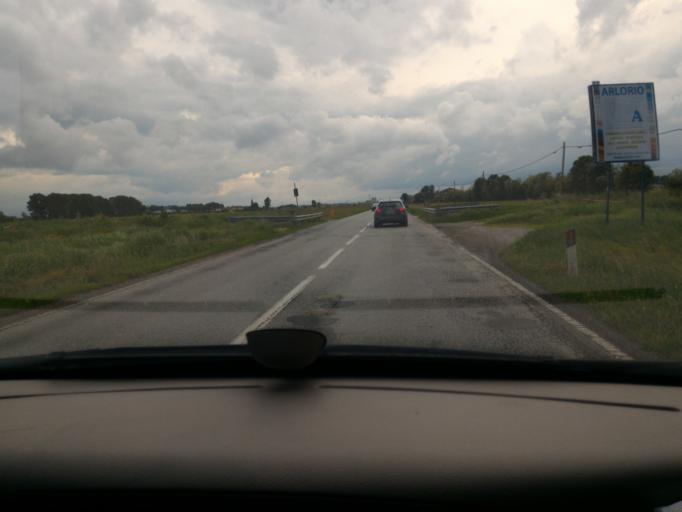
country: IT
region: Piedmont
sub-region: Provincia di Cuneo
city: Savigliano
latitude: 44.6241
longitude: 7.6655
